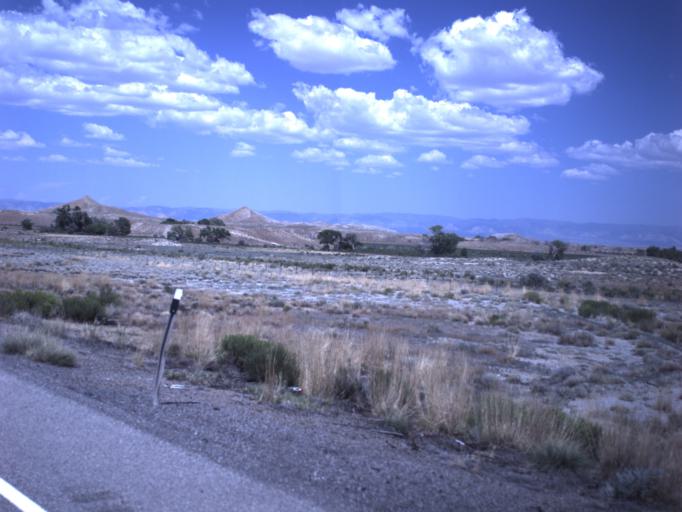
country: US
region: Utah
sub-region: Emery County
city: Huntington
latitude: 39.4277
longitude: -110.8692
